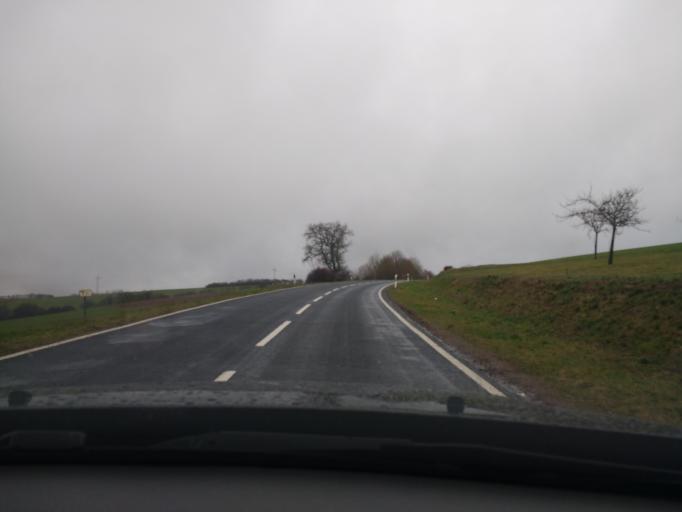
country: DE
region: Rheinland-Pfalz
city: Gusterath
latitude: 49.7029
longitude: 6.7104
